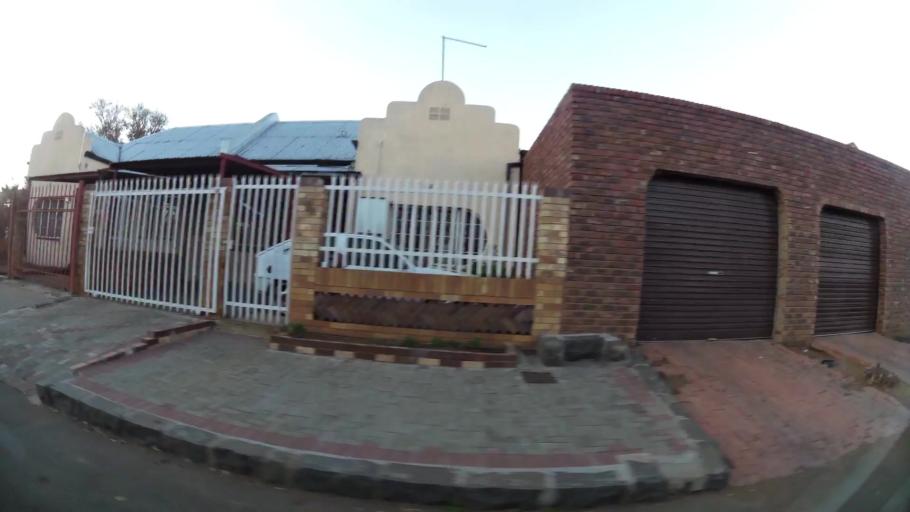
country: ZA
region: Northern Cape
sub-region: Frances Baard District Municipality
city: Kimberley
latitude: -28.7320
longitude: 24.7676
